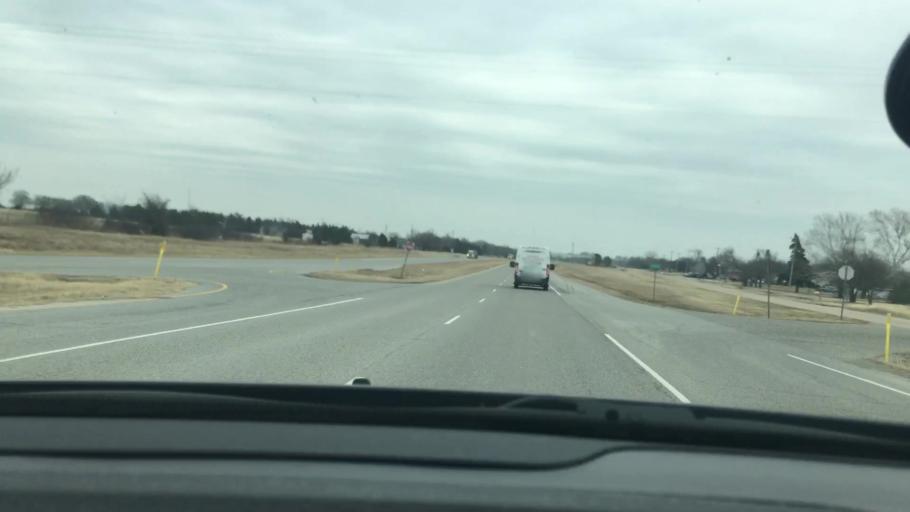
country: US
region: Oklahoma
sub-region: Carter County
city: Wilson
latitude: 34.1730
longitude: -97.4398
